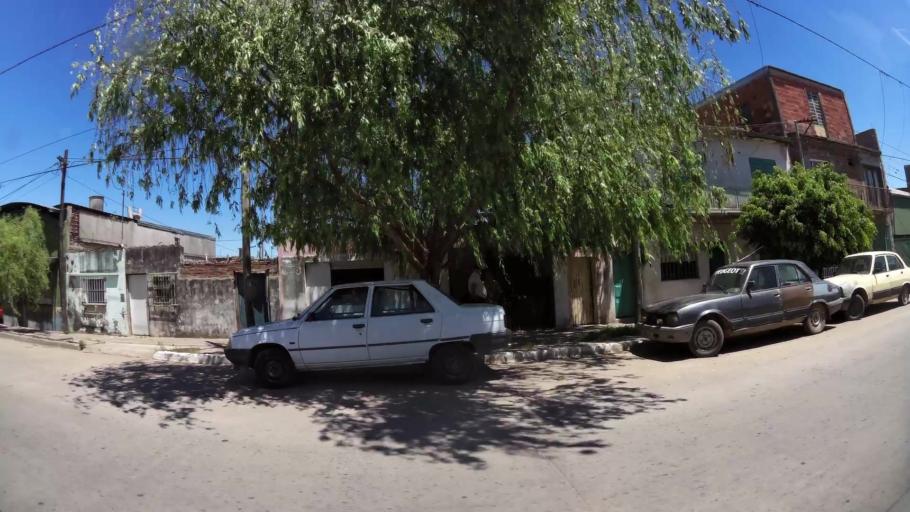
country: AR
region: Santa Fe
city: Santa Fe de la Vera Cruz
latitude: -31.6226
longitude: -60.7186
